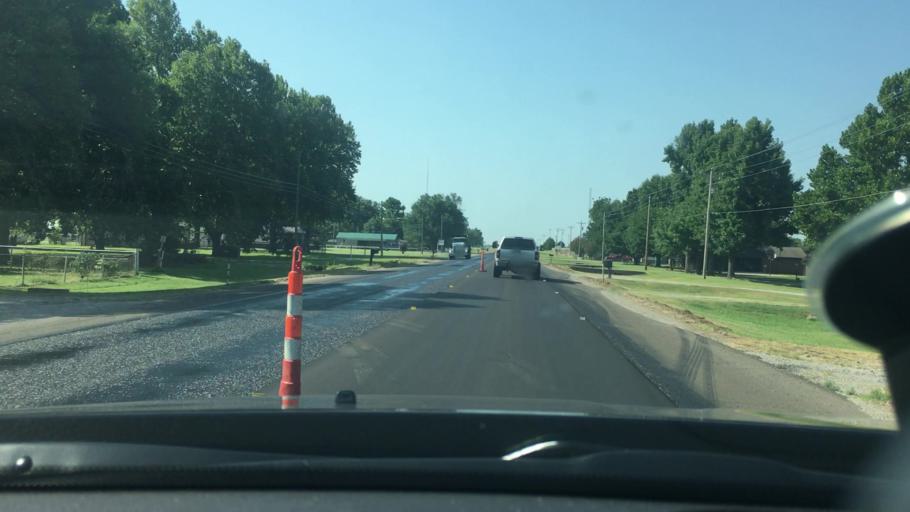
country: US
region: Oklahoma
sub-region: Garvin County
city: Lindsay
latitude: 34.8082
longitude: -97.5983
